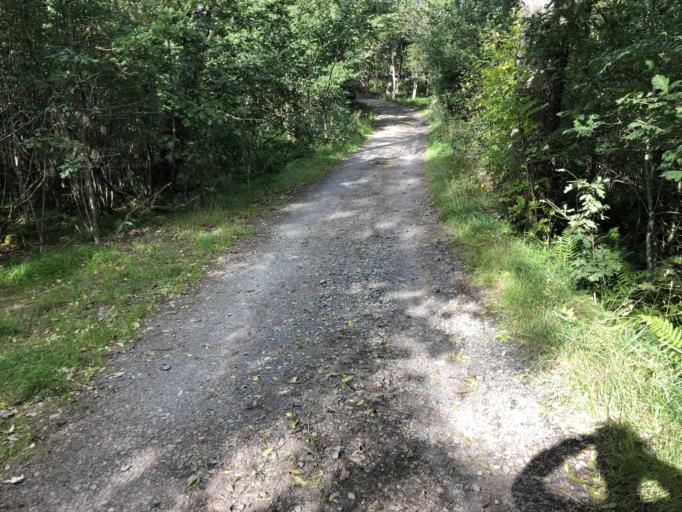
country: SE
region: Vaestra Goetaland
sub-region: Goteborg
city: Majorna
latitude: 57.7500
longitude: 11.8661
